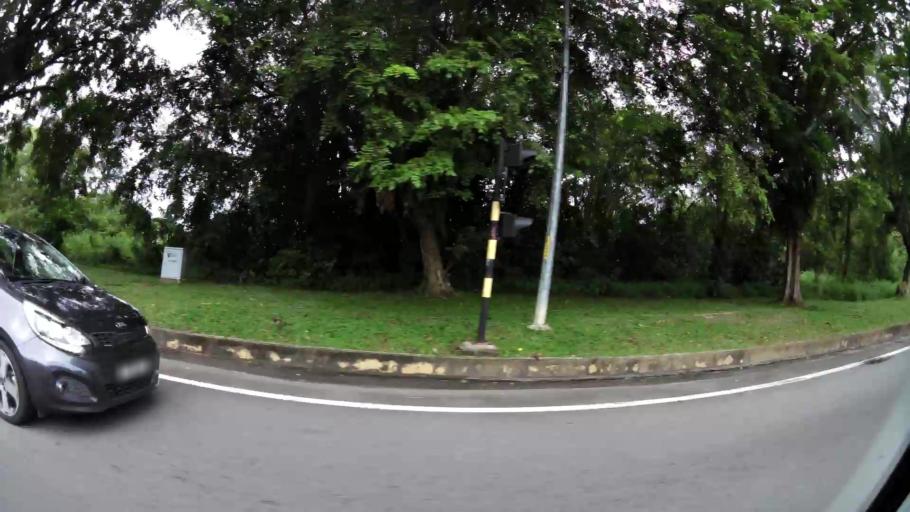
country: BN
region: Brunei and Muara
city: Bandar Seri Begawan
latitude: 4.9108
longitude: 114.9312
